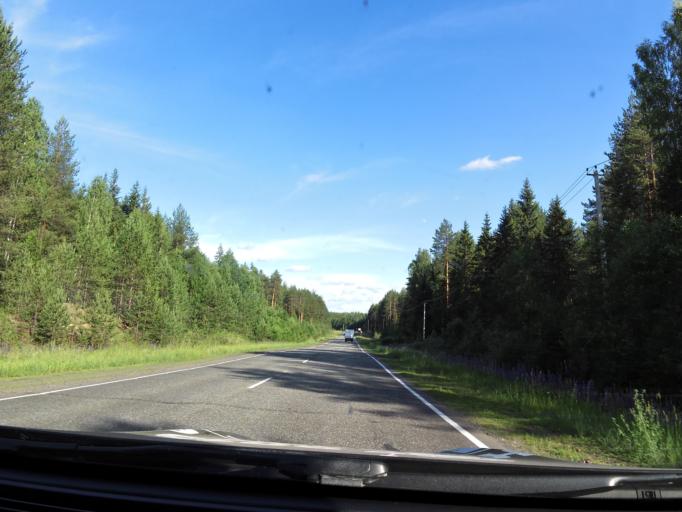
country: RU
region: Kirov
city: Dubrovka
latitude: 58.9068
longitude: 51.1833
